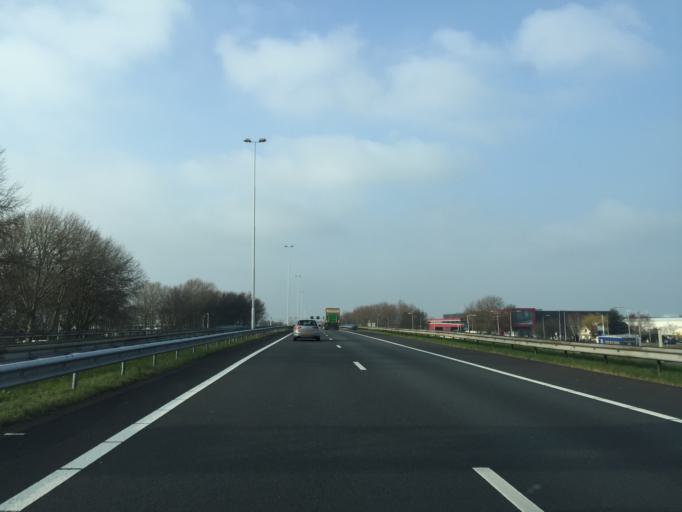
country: NL
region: South Holland
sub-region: Gemeente Westland
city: Maasdijk
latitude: 51.9512
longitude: 4.2328
